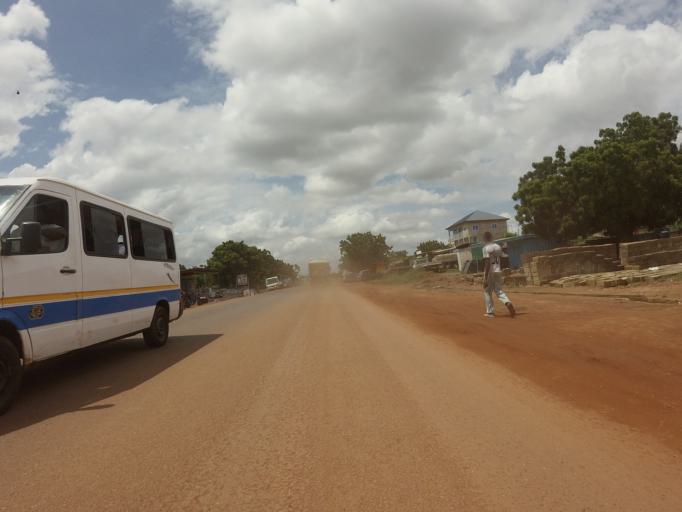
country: GH
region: Eastern
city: Aburi
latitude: 5.8145
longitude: -0.1219
